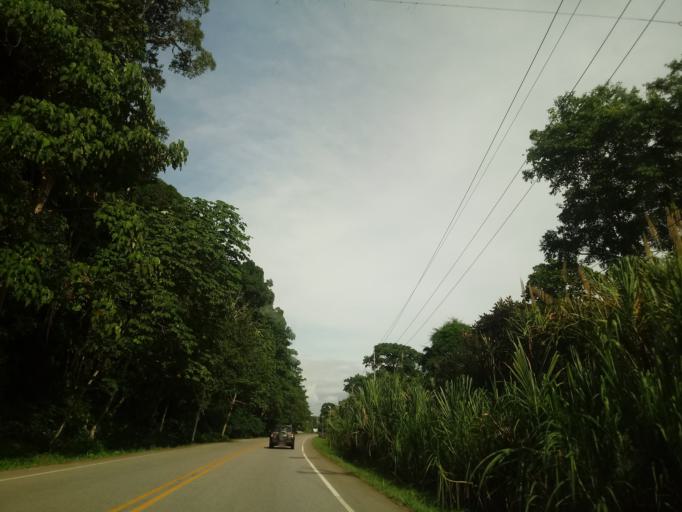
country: CR
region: San Jose
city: Daniel Flores
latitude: 9.1949
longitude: -83.7807
